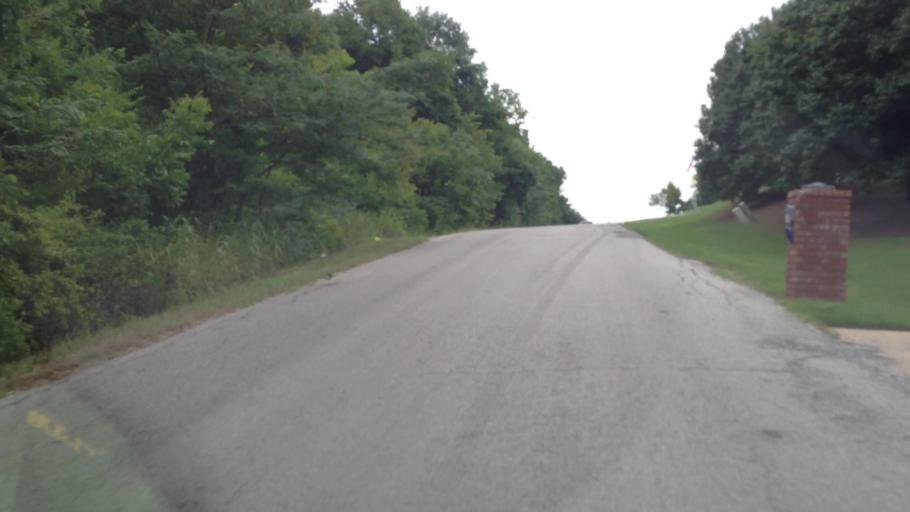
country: US
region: Oklahoma
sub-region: Craig County
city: Vinita
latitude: 36.6282
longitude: -95.1257
